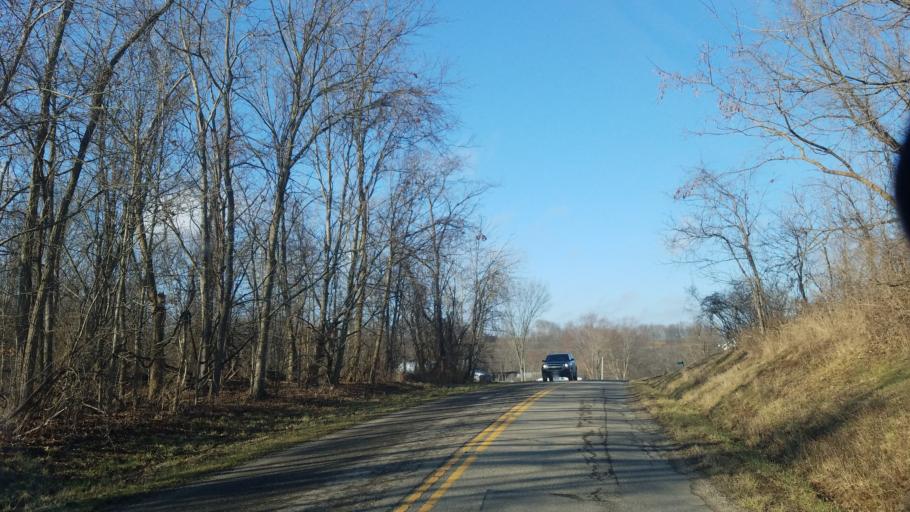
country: US
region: Ohio
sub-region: Guernsey County
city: Byesville
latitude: 40.0360
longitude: -81.4071
